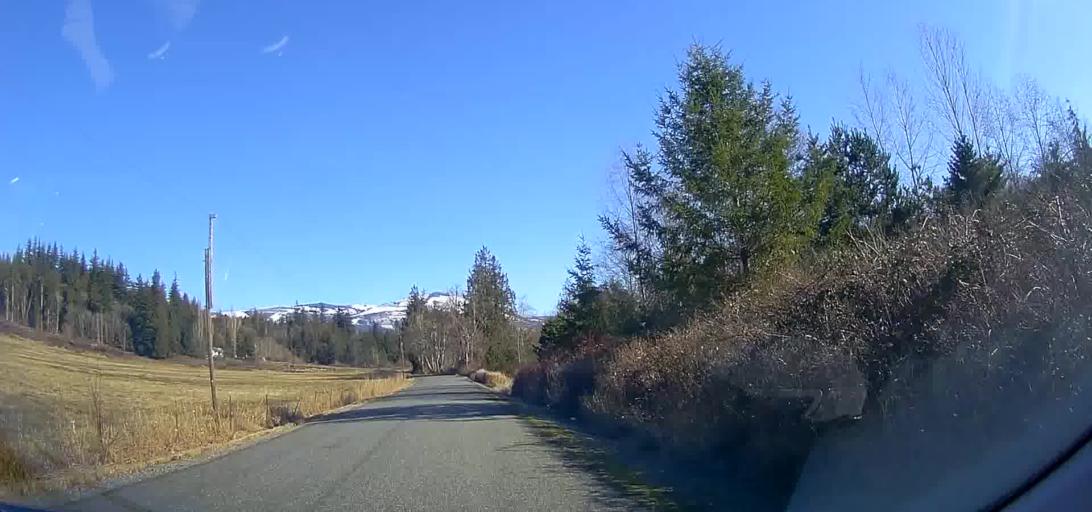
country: US
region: Washington
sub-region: Skagit County
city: Clear Lake
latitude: 48.4473
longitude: -122.2560
